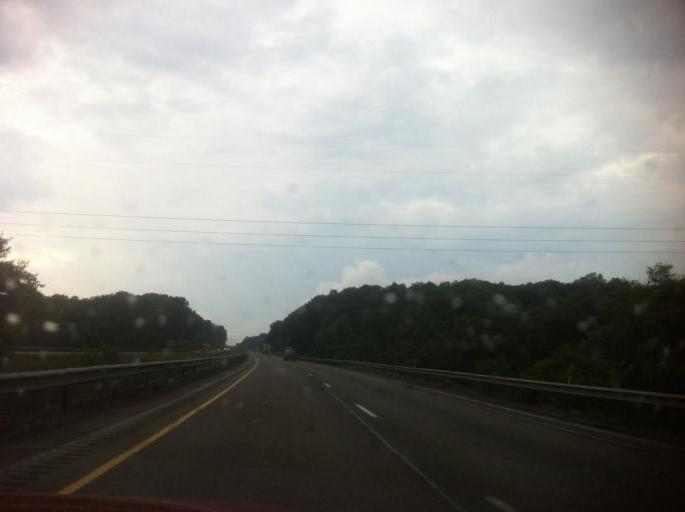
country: US
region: Pennsylvania
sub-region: Jefferson County
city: Brookville
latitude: 41.1608
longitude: -79.0021
